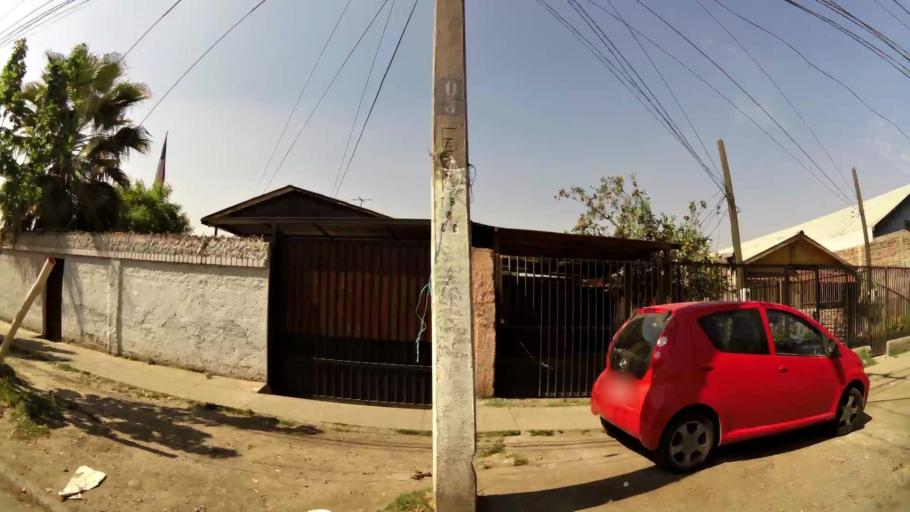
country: CL
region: Santiago Metropolitan
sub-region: Provincia de Santiago
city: La Pintana
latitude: -33.5471
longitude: -70.6079
